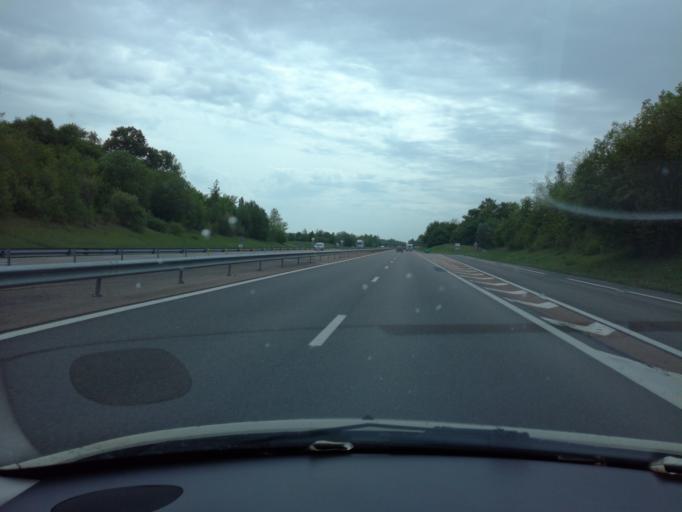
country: FR
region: Franche-Comte
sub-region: Departement du Jura
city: Mont-sous-Vaudrey
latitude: 46.8729
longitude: 5.5822
